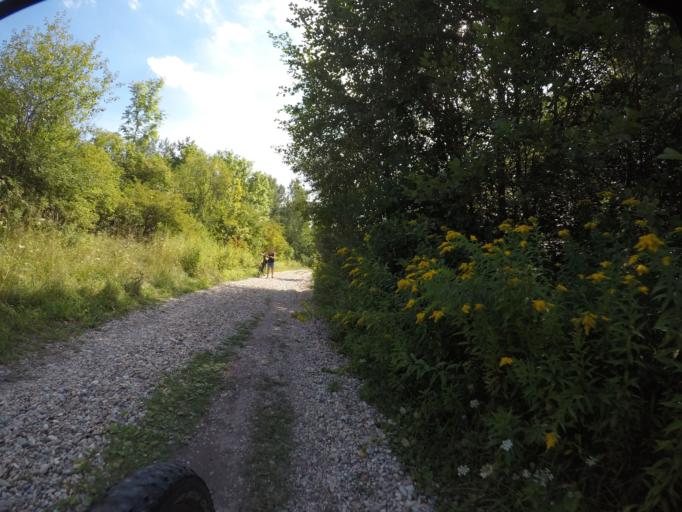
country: AT
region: Lower Austria
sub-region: Politischer Bezirk Wien-Umgebung
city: Schwechat
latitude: 48.1903
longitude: 16.4839
